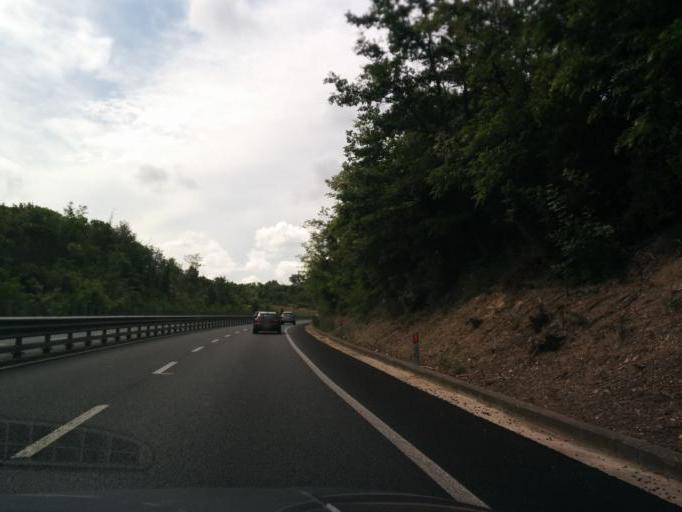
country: IT
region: Tuscany
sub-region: Province of Florence
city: Sambuca
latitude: 43.5406
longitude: 11.2195
